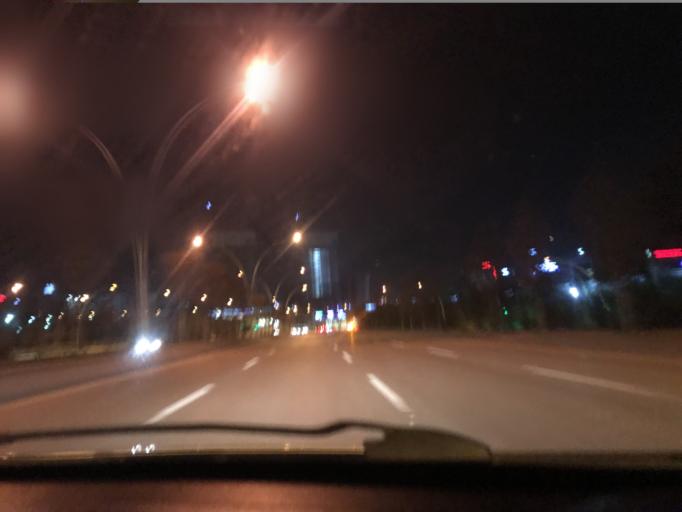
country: TR
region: Ankara
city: Ankara
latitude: 39.9042
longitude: 32.7876
